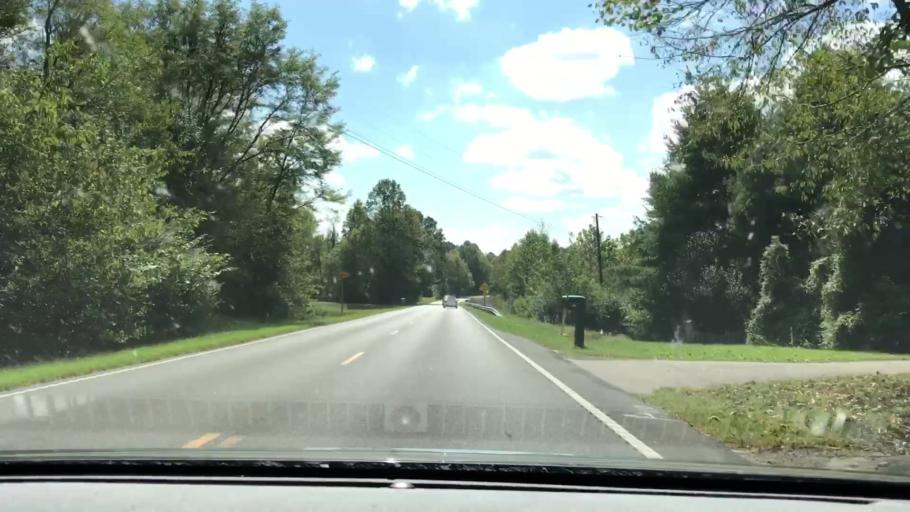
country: US
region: Kentucky
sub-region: McCracken County
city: Reidland
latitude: 36.9772
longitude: -88.5155
